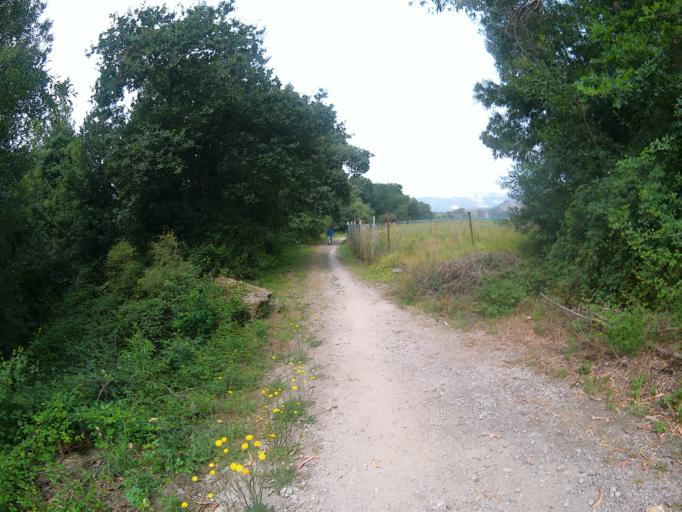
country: PT
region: Viana do Castelo
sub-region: Ponte de Lima
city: Ponte de Lima
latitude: 41.7753
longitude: -8.5601
